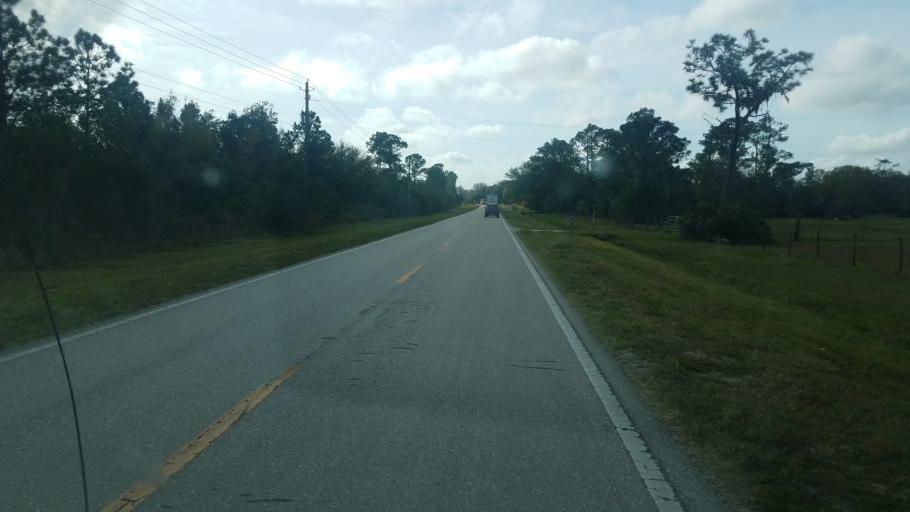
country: US
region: Florida
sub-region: Polk County
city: Polk City
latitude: 28.2116
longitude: -81.7567
